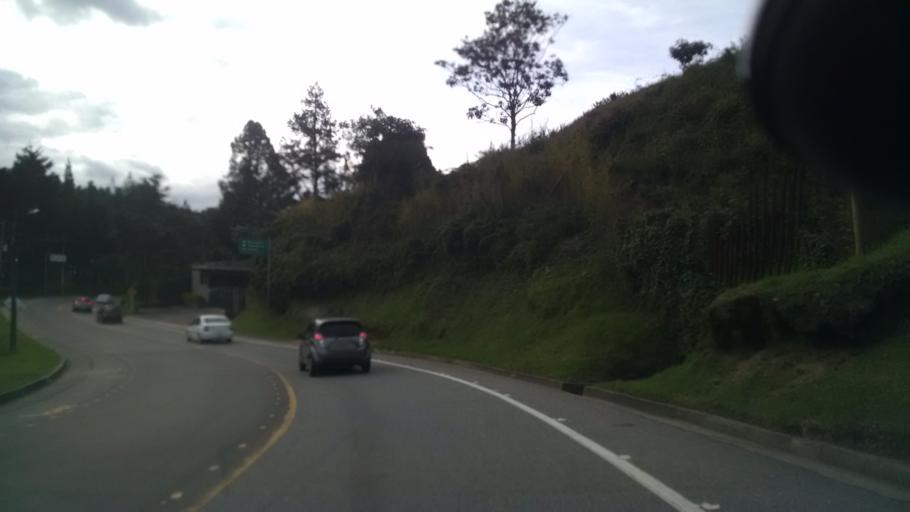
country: CO
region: Antioquia
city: Envigado
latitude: 6.1418
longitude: -75.5224
